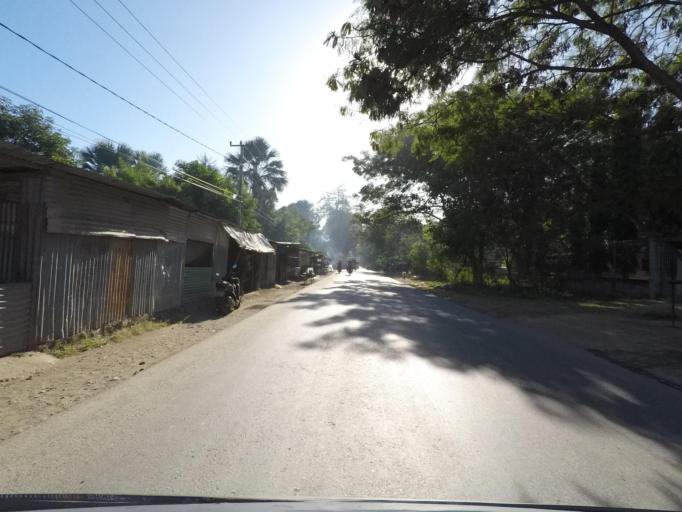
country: ID
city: Metinaro
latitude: -8.5506
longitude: 125.6629
